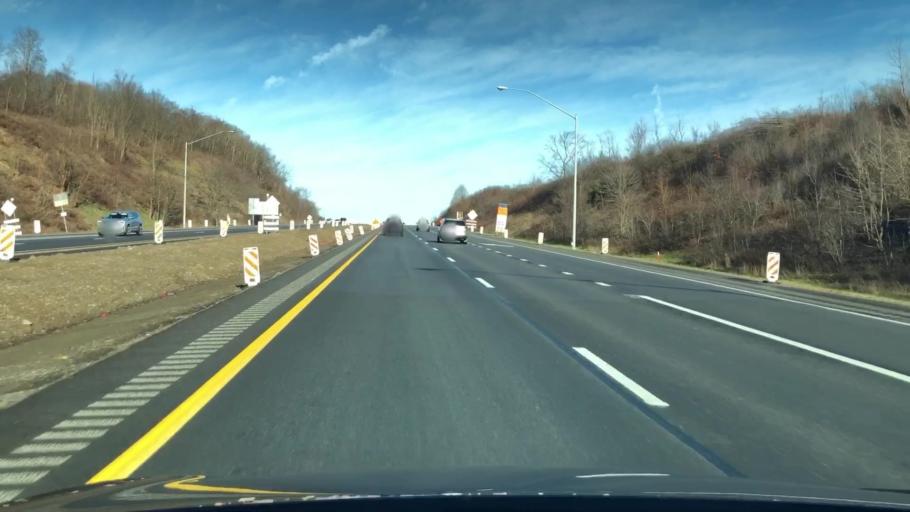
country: US
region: Pennsylvania
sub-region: Allegheny County
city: Brackenridge
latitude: 40.6160
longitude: -79.7532
